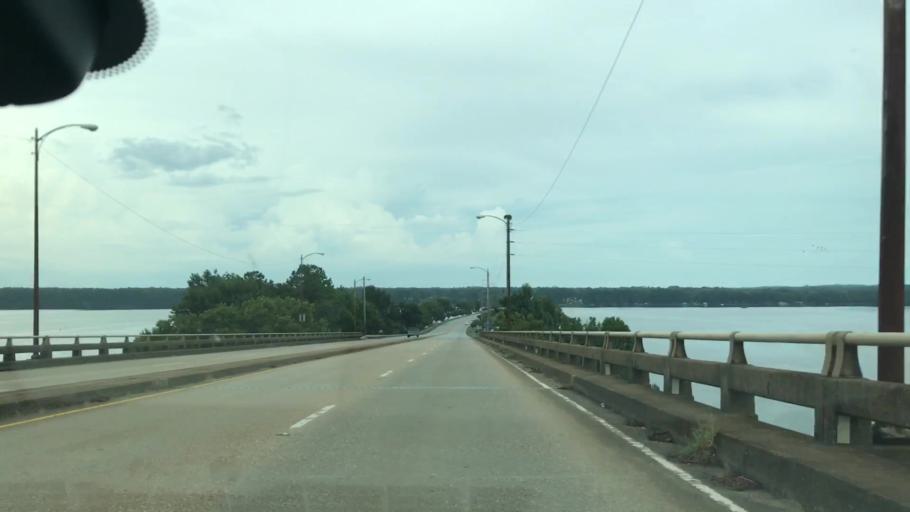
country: US
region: Alabama
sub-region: Barbour County
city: Eufaula
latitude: 31.8913
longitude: -85.1332
